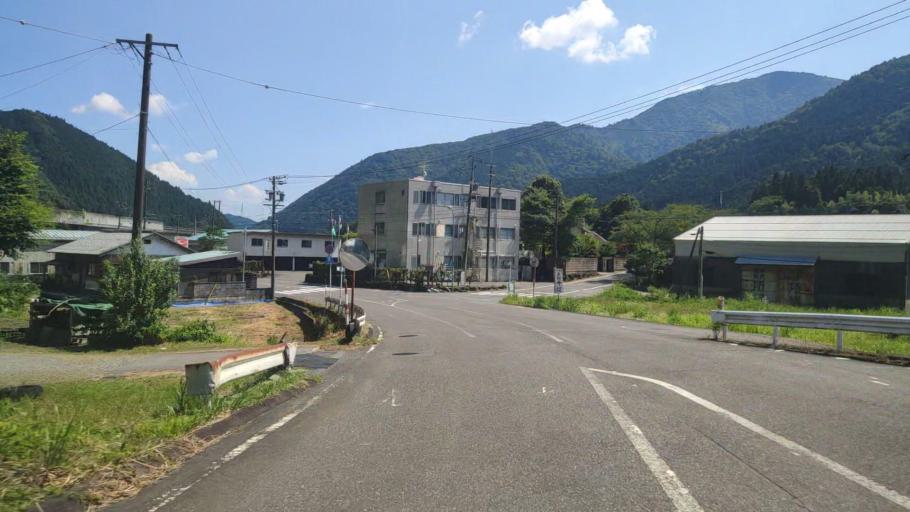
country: JP
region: Gifu
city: Godo
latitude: 35.6258
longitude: 136.6196
